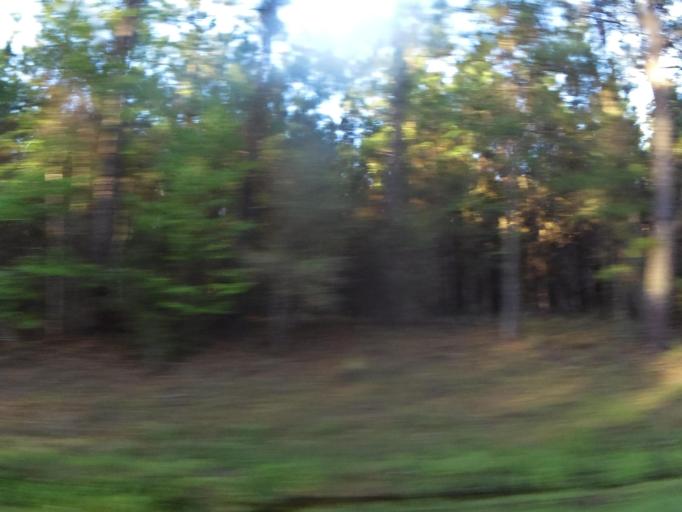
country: US
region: Florida
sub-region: Clay County
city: Keystone Heights
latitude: 29.8505
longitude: -82.0931
